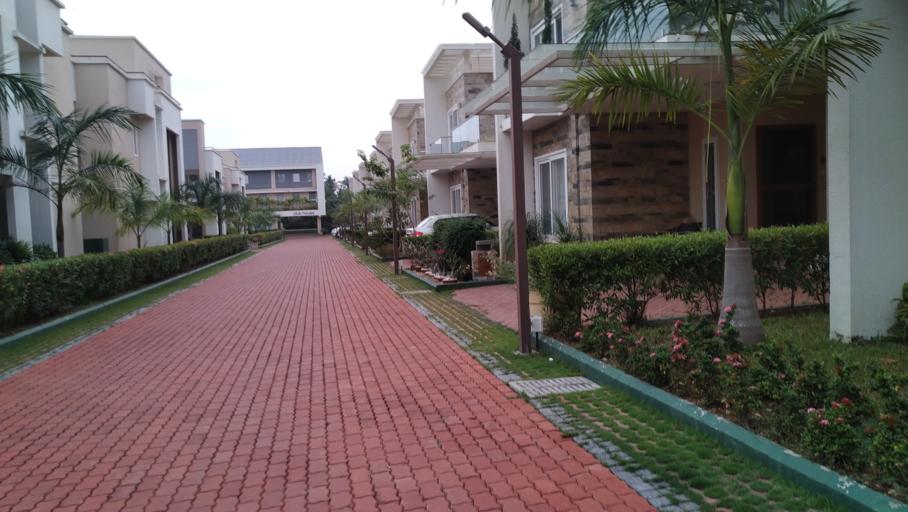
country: IN
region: Kerala
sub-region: Ernakulam
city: Aluva
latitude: 10.0918
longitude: 76.3590
